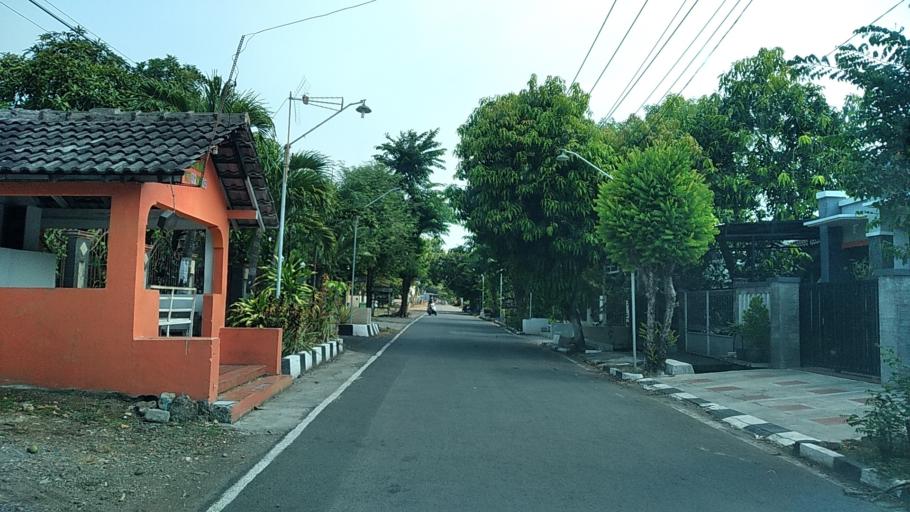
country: ID
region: Central Java
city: Mranggen
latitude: -7.0474
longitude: 110.4810
